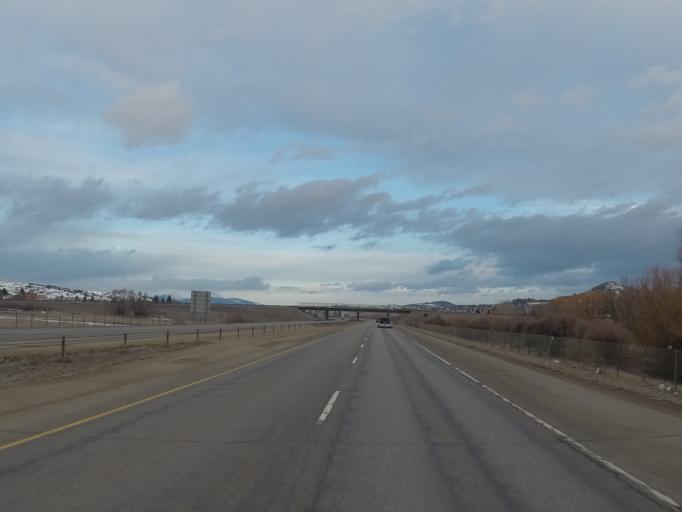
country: US
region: Montana
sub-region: Silver Bow County
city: Butte
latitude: 45.9902
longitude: -112.5254
